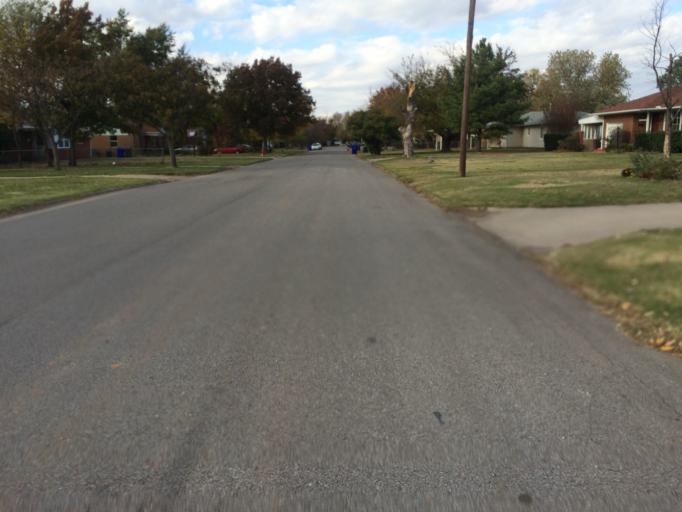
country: US
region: Oklahoma
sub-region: Cleveland County
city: Norman
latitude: 35.2363
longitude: -97.4516
